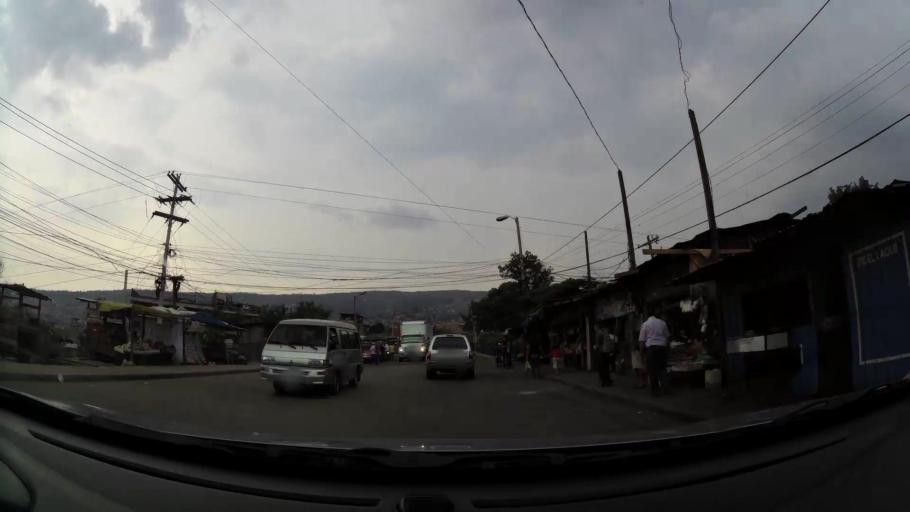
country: HN
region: Francisco Morazan
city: El Lolo
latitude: 14.1021
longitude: -87.2406
